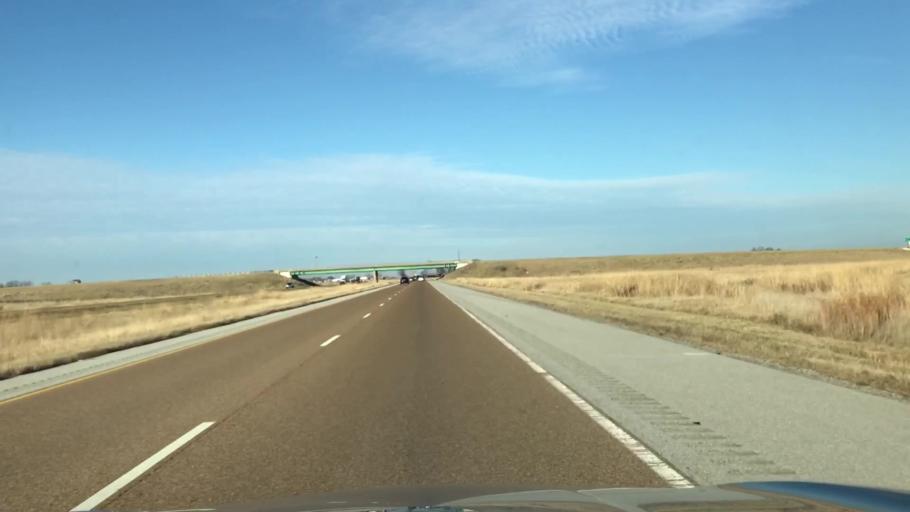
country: US
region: Illinois
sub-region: Macoupin County
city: Staunton
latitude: 39.0178
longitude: -89.7494
